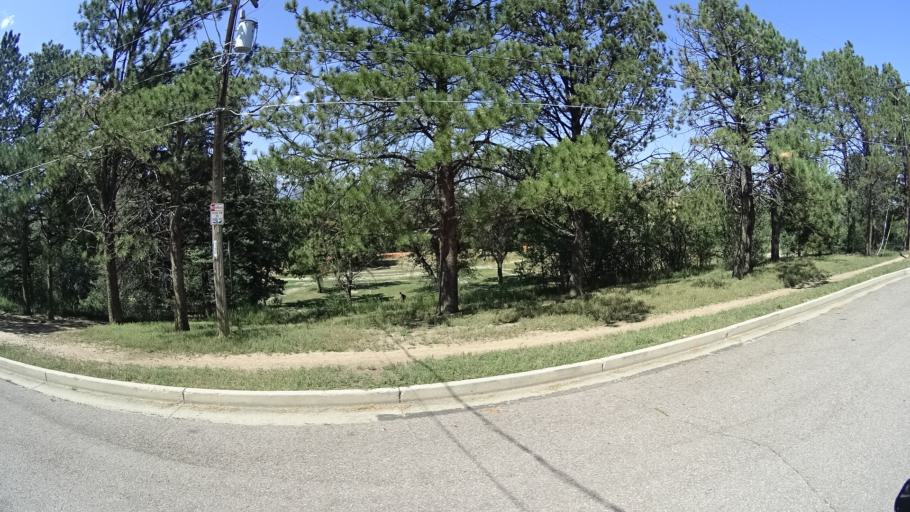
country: US
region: Colorado
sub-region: El Paso County
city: Colorado Springs
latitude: 38.8583
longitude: -104.8302
